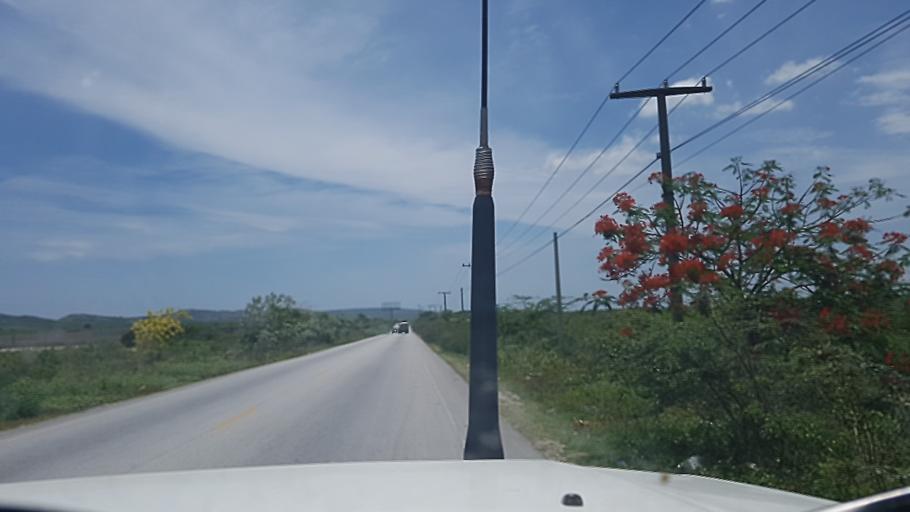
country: HT
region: Artibonite
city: Saint-Marc
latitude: 19.1519
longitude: -72.6289
